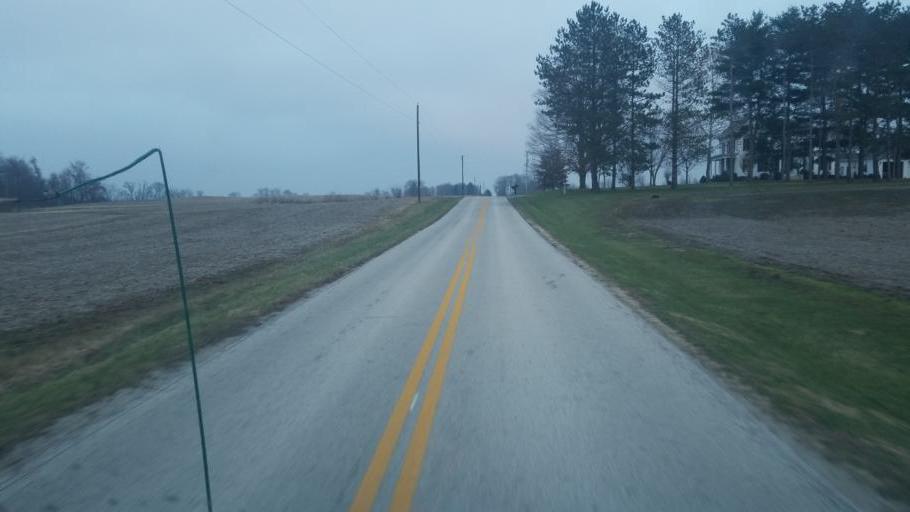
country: US
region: Ohio
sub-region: Seneca County
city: Tiffin
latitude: 40.9929
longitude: -83.2268
